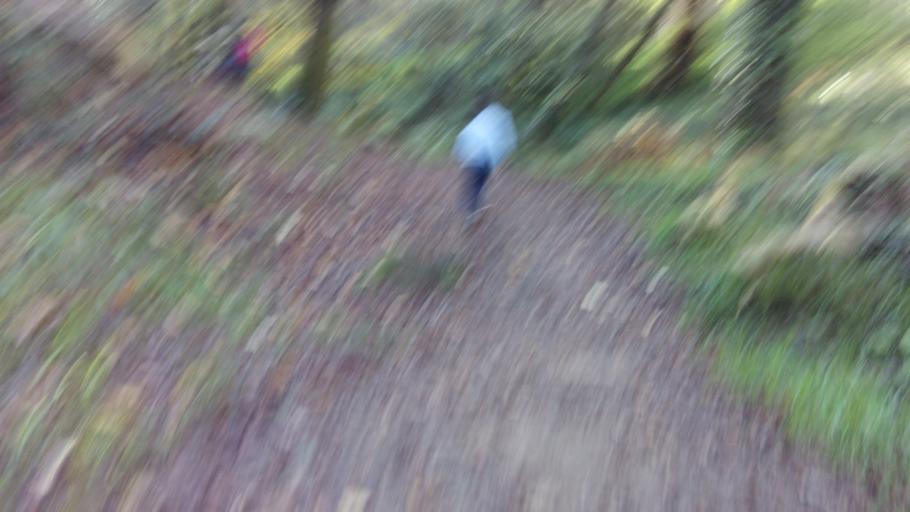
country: ES
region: Galicia
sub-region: Provincia de Pontevedra
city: Meis
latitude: 42.4757
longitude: -8.7432
